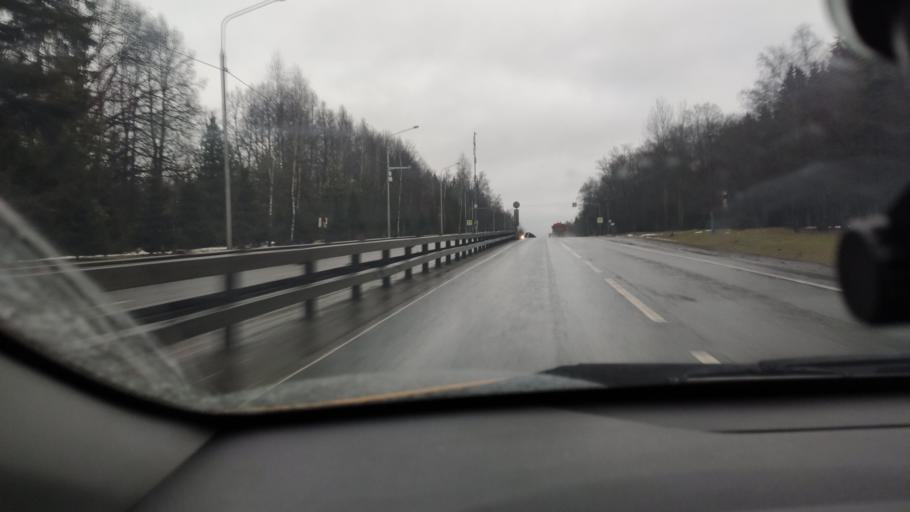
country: RU
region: Moskovskaya
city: Troitsk
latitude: 55.3431
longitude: 37.3154
